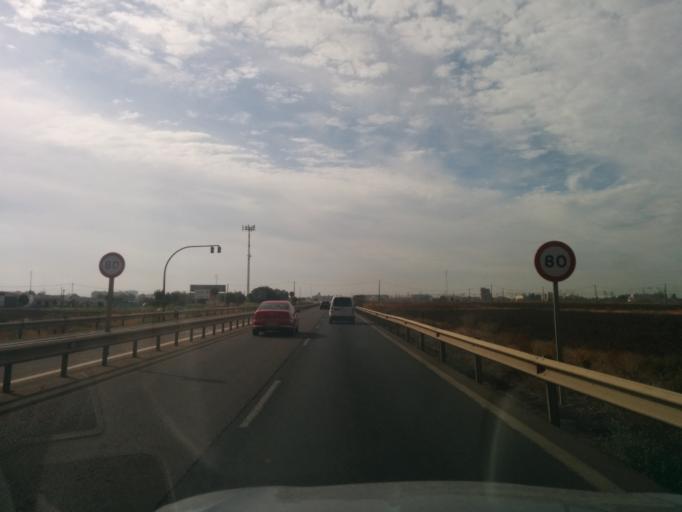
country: ES
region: Andalusia
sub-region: Provincia de Sevilla
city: Sevilla
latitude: 37.4216
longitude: -5.9470
